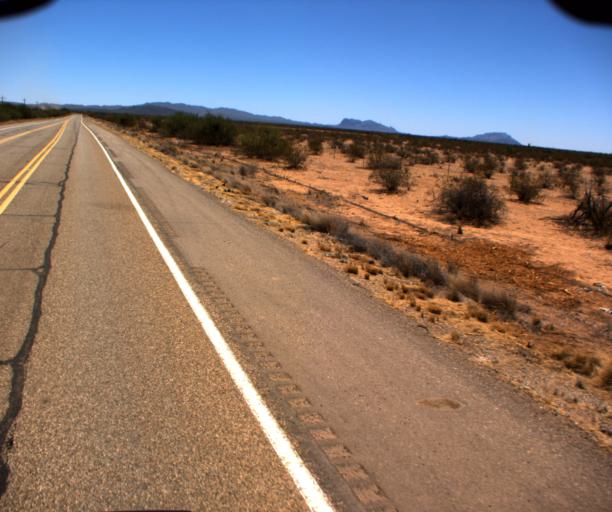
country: US
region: Arizona
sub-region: Pima County
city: Ajo
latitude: 32.1836
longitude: -112.3565
